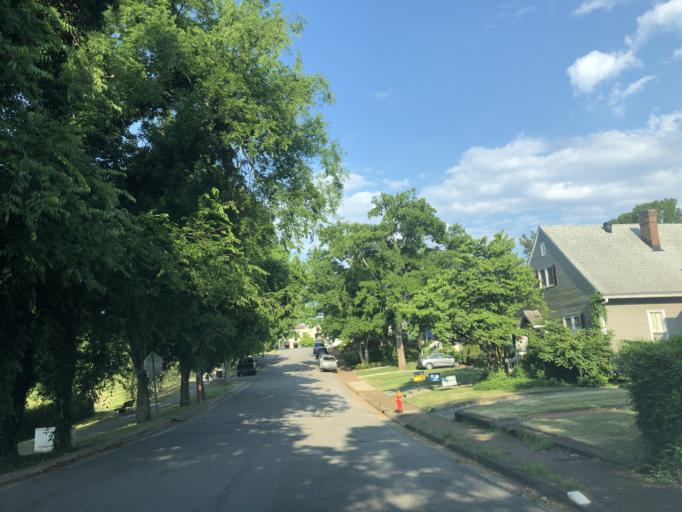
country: US
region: Tennessee
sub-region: Davidson County
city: Nashville
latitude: 36.1315
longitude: -86.8034
